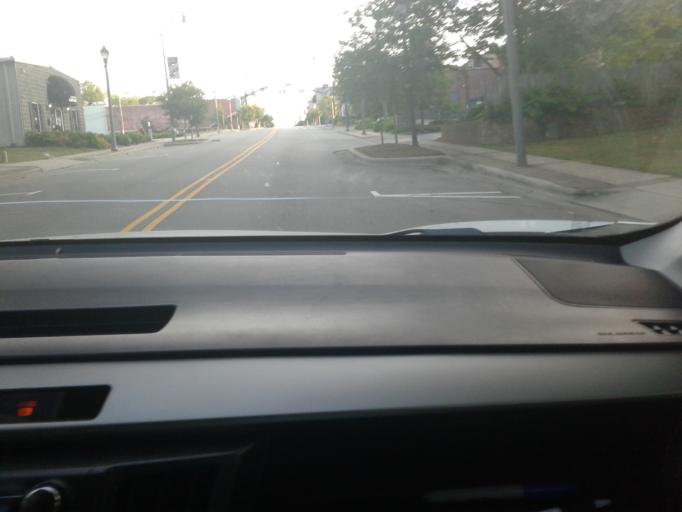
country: US
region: North Carolina
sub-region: Wake County
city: Fuquay-Varina
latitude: 35.5809
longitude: -78.7997
